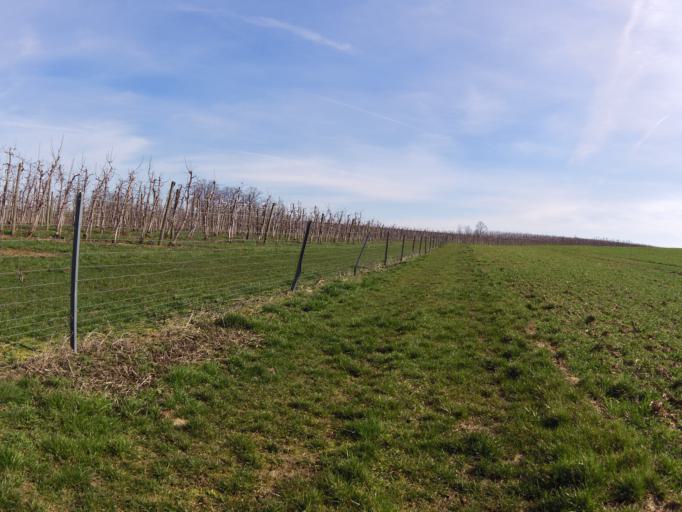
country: DE
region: Bavaria
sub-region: Regierungsbezirk Unterfranken
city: Biebelried
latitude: 49.8021
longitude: 10.0734
